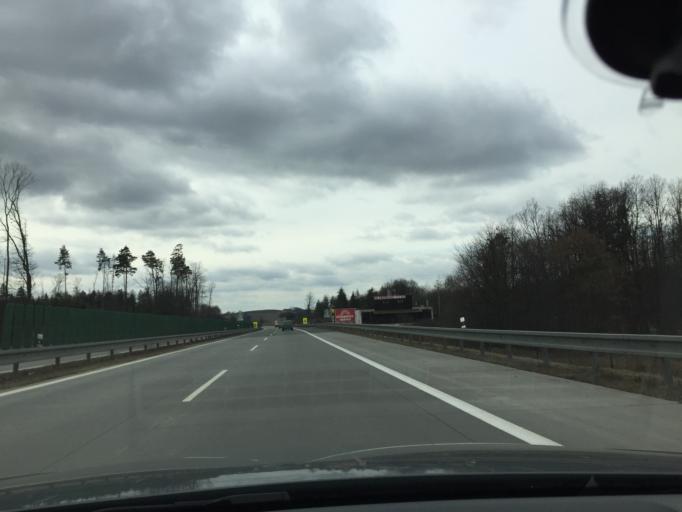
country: CZ
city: Frycovice
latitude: 49.6560
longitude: 18.2496
